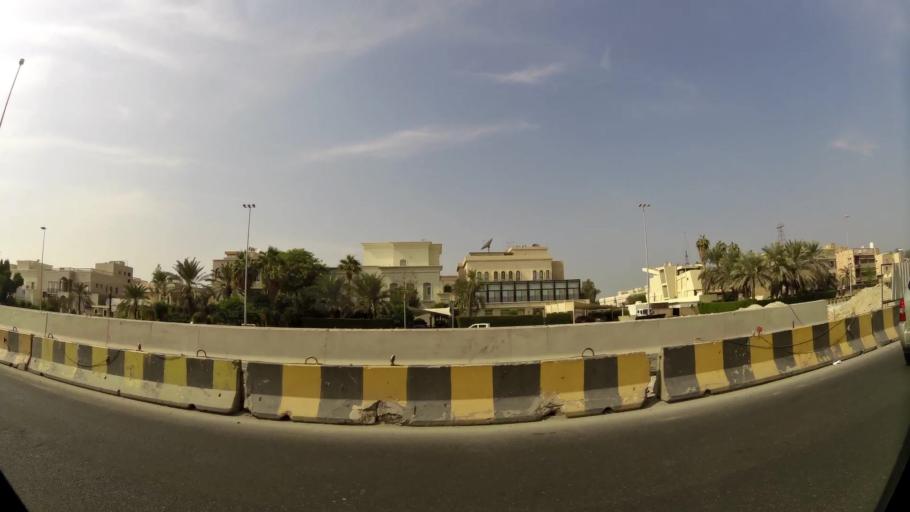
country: KW
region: Al Asimah
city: Ash Shamiyah
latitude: 29.3507
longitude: 47.9583
